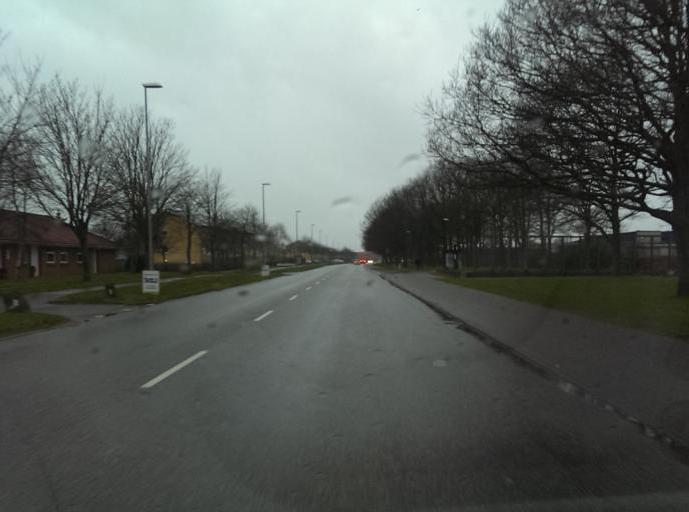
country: DK
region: South Denmark
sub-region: Esbjerg Kommune
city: Esbjerg
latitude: 55.4870
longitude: 8.4837
